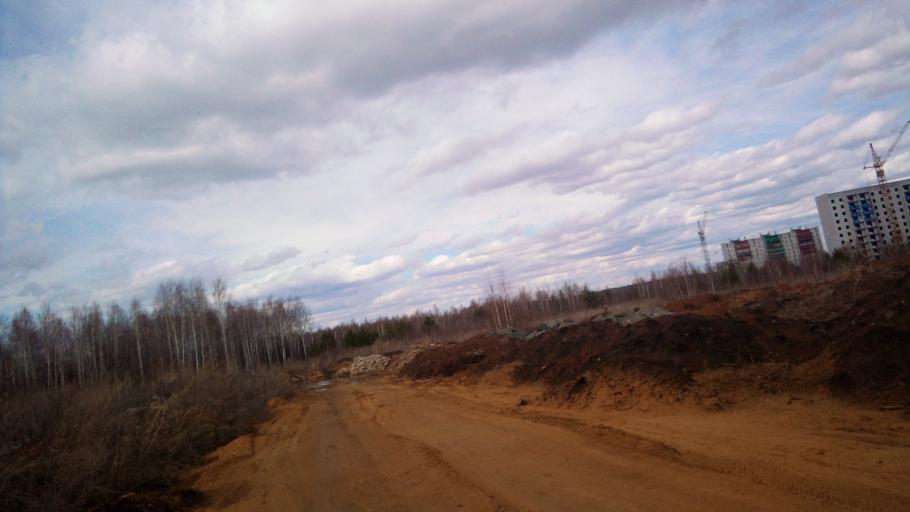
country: RU
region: Chelyabinsk
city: Sargazy
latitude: 55.1261
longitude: 61.2576
